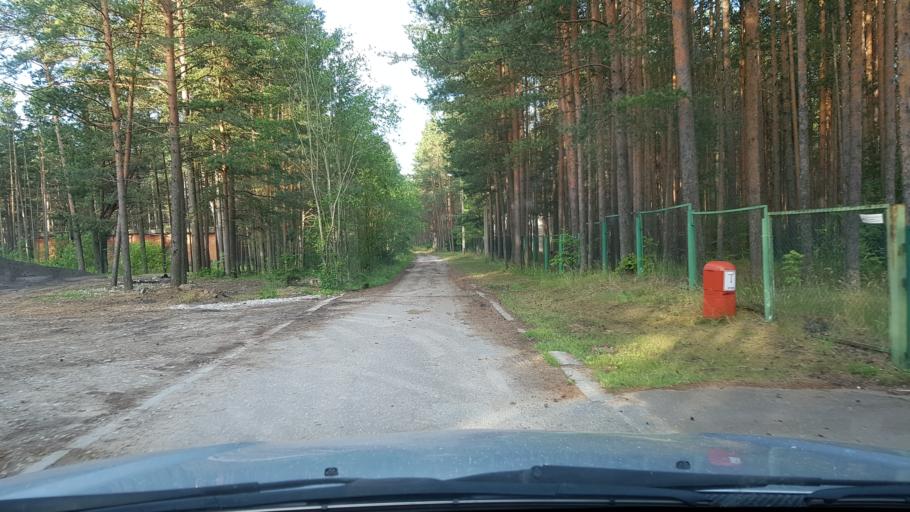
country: EE
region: Ida-Virumaa
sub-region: Narva-Joesuu linn
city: Narva-Joesuu
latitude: 59.4543
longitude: 28.0458
